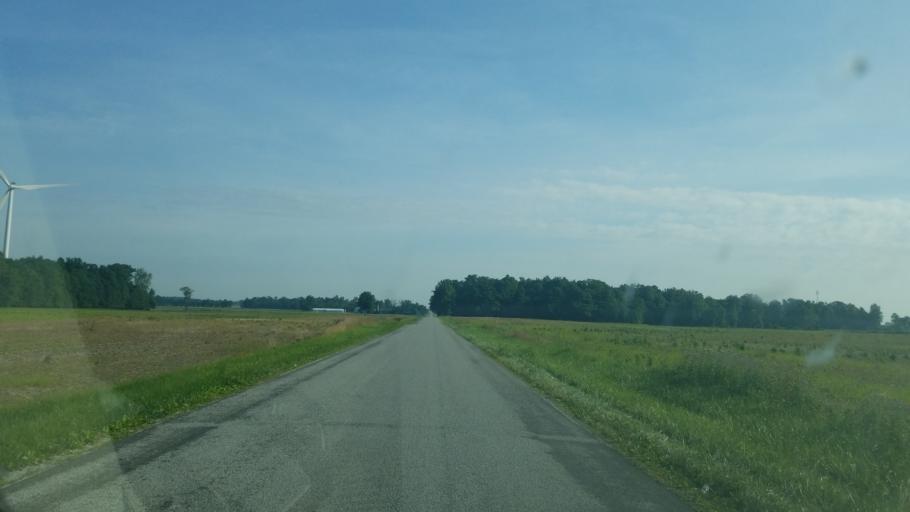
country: US
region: Ohio
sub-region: Hancock County
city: Arlington
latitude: 40.7911
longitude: -83.6708
